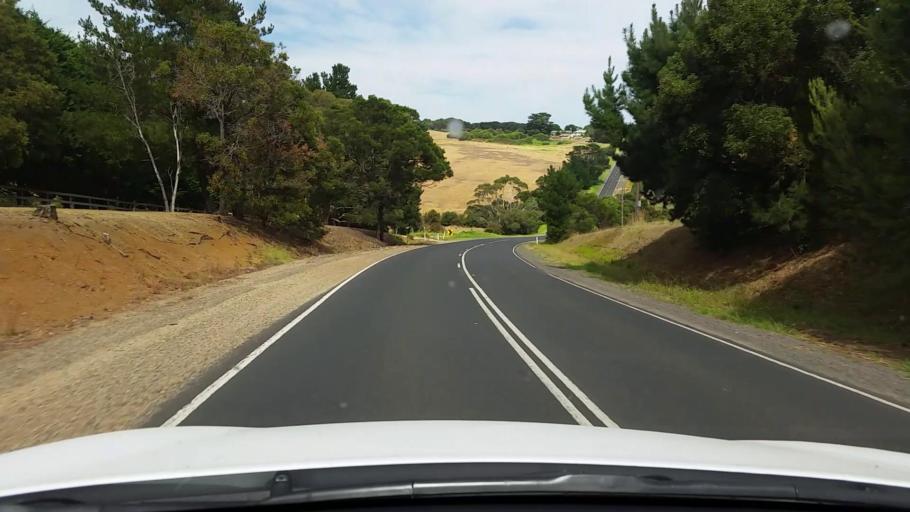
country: AU
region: Victoria
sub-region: Mornington Peninsula
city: Merricks
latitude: -38.4488
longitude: 145.0305
